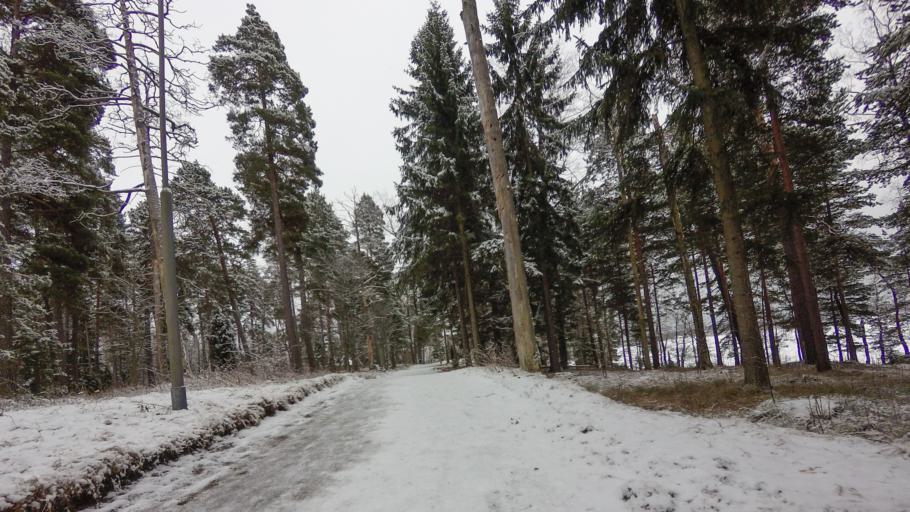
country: FI
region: Uusimaa
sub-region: Helsinki
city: Teekkarikylae
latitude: 60.1778
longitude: 24.8810
